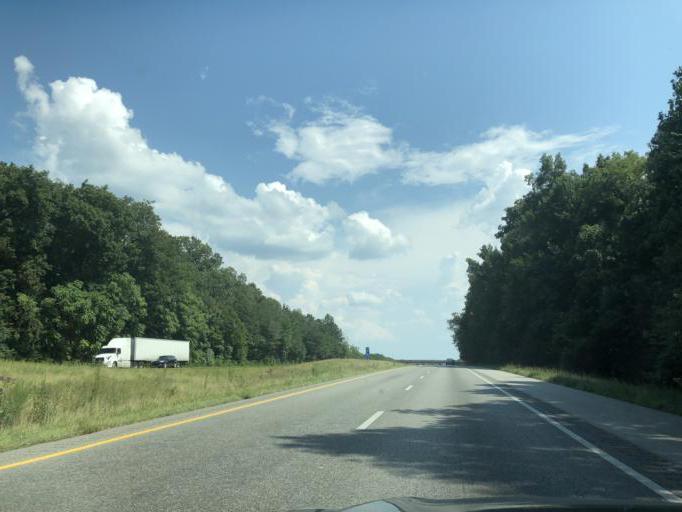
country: US
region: Tennessee
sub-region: Franklin County
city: Sewanee
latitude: 35.3663
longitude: -85.9651
